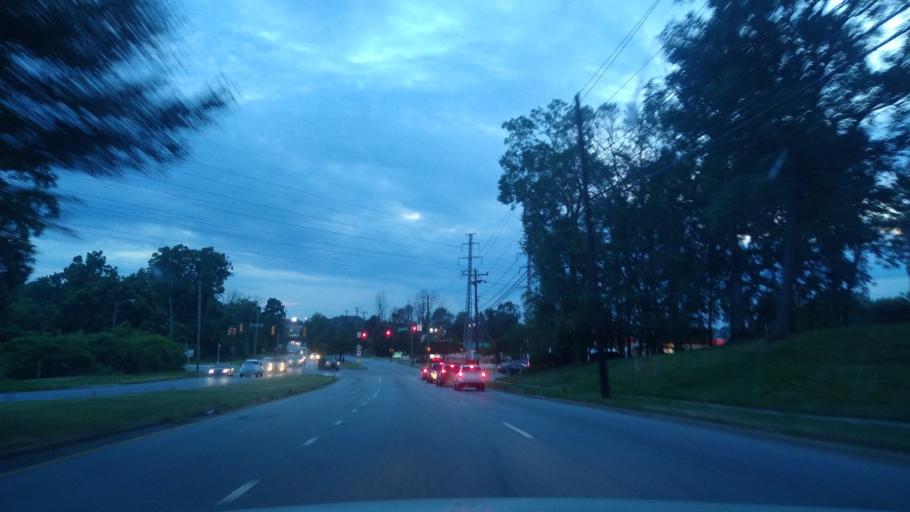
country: US
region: North Carolina
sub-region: Guilford County
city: Greensboro
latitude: 36.1134
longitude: -79.7744
